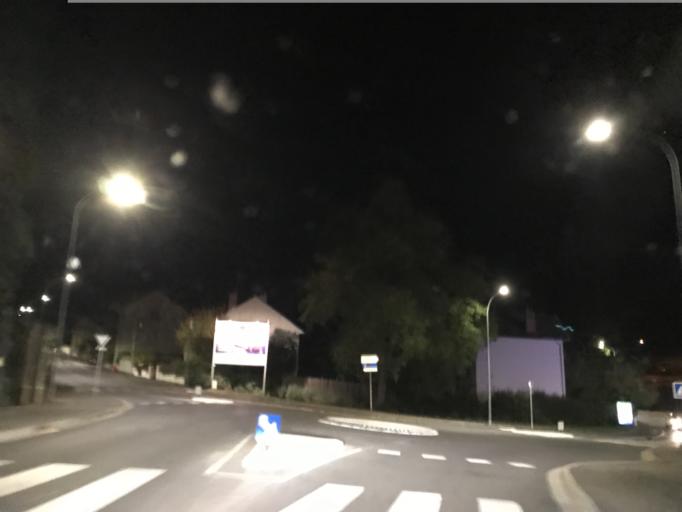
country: FR
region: Auvergne
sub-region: Departement de l'Allier
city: Vichy
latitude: 46.1197
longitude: 3.4352
